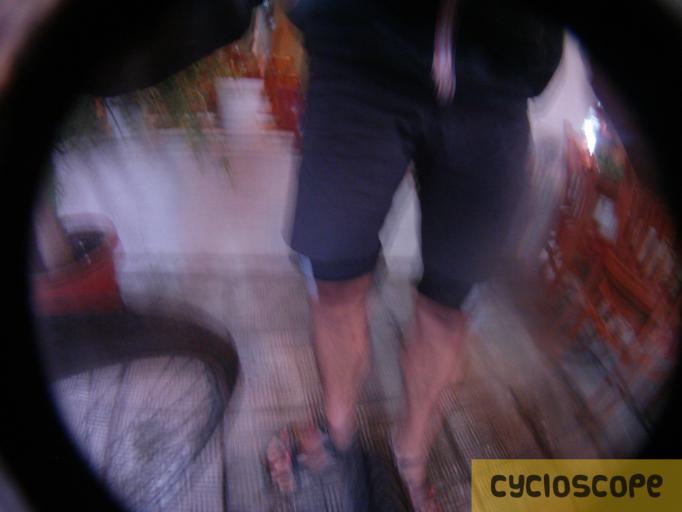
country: BG
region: Shumen
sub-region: Obshtina Khitrino
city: Gara Khitrino
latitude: 43.3642
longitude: 26.8486
